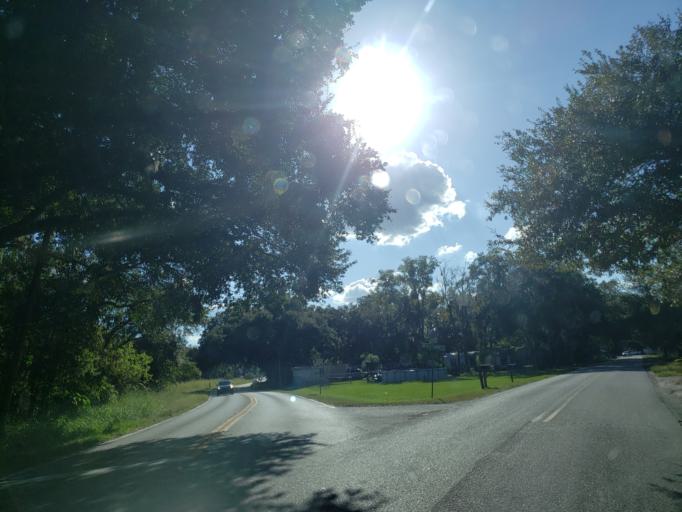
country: US
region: Florida
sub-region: Hillsborough County
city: Dover
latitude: 27.9780
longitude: -82.1845
